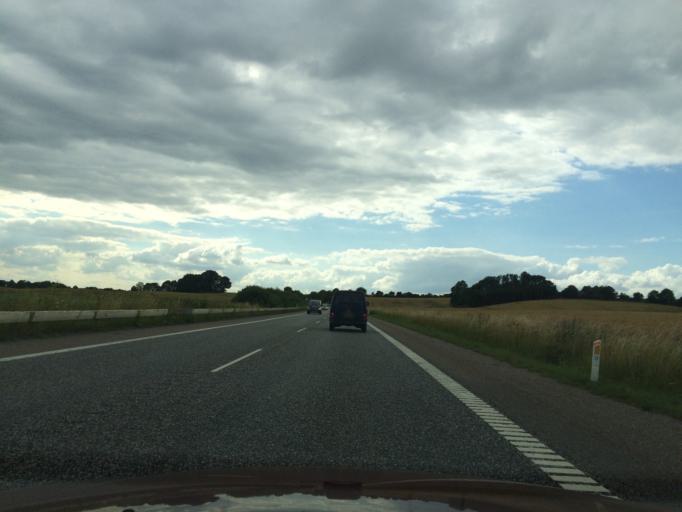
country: DK
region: Central Jutland
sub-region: Syddjurs Kommune
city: Ronde
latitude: 56.3178
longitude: 10.4730
